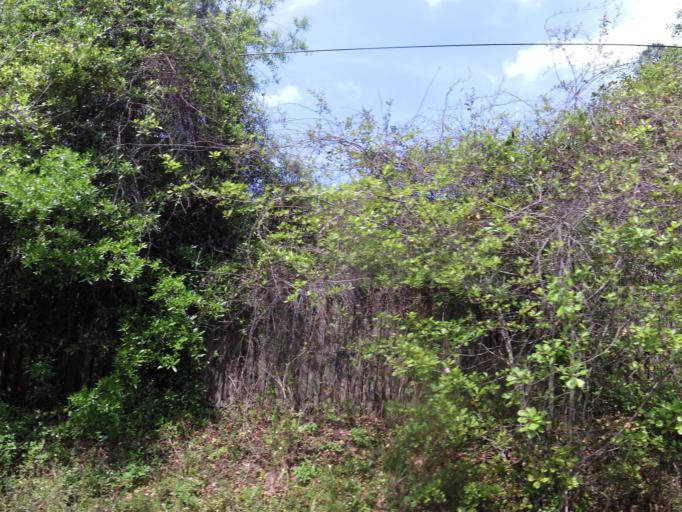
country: US
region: Georgia
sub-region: Camden County
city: Kingsland
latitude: 30.7841
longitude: -81.6992
